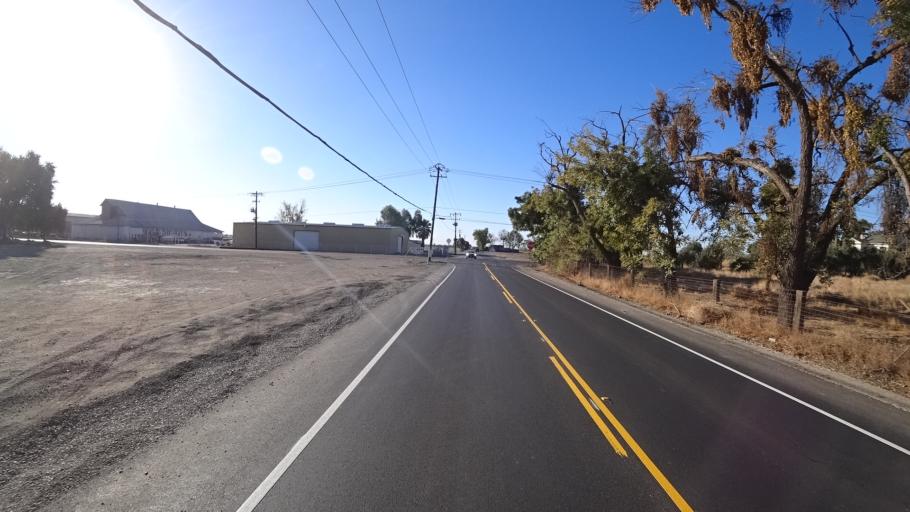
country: US
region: California
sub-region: Yolo County
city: Woodland
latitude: 38.6199
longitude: -121.7850
